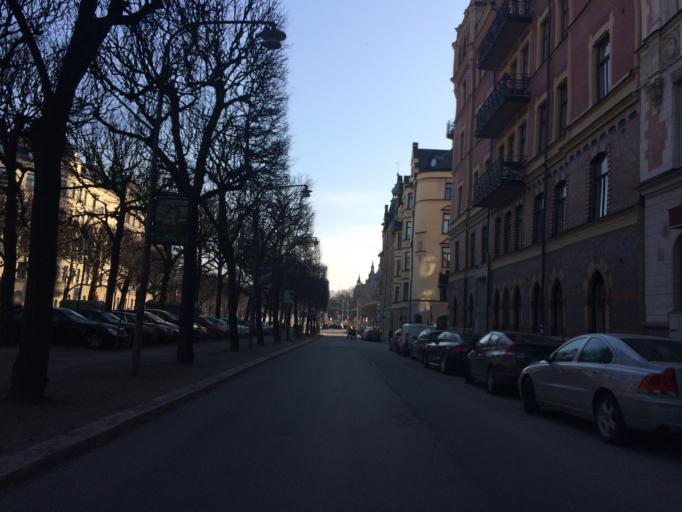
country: SE
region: Stockholm
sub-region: Stockholms Kommun
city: OEstermalm
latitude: 59.3331
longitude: 18.0924
